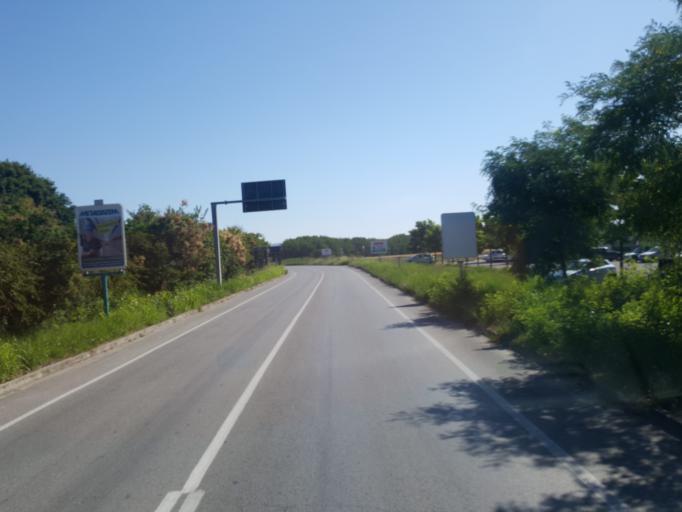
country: IT
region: The Marches
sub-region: Provincia di Pesaro e Urbino
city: Borgo Santa Maria
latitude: 43.8724
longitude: 12.8046
